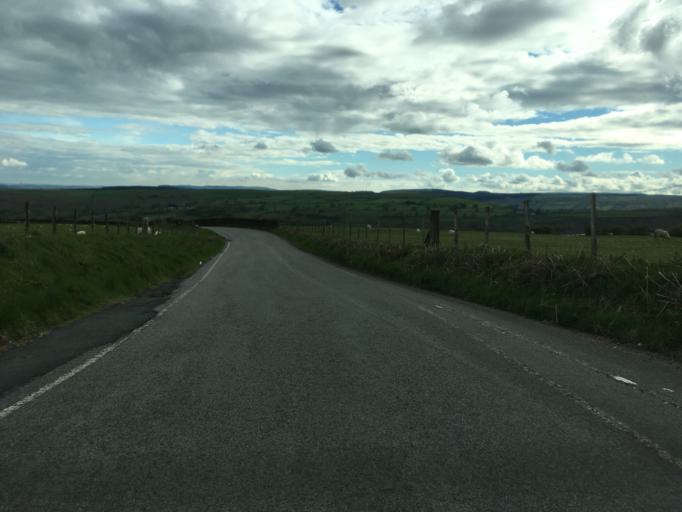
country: GB
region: Wales
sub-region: Merthyr Tydfil County Borough
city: Treharris
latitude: 51.7132
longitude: -3.3088
